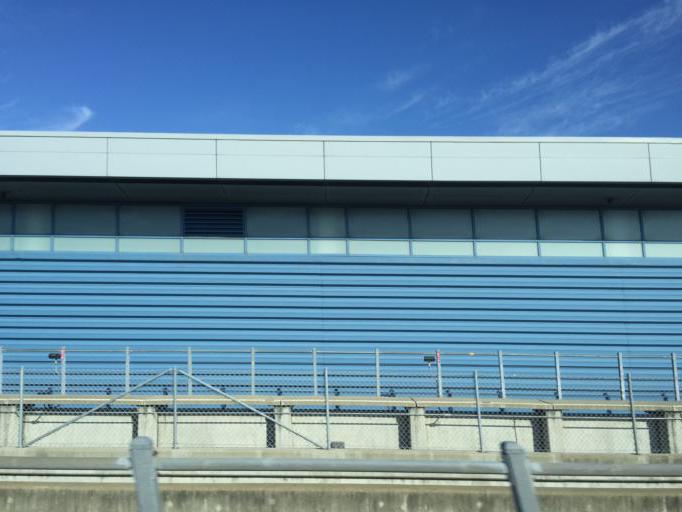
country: US
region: California
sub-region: San Mateo County
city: San Bruno
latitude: 37.6236
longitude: -122.4000
